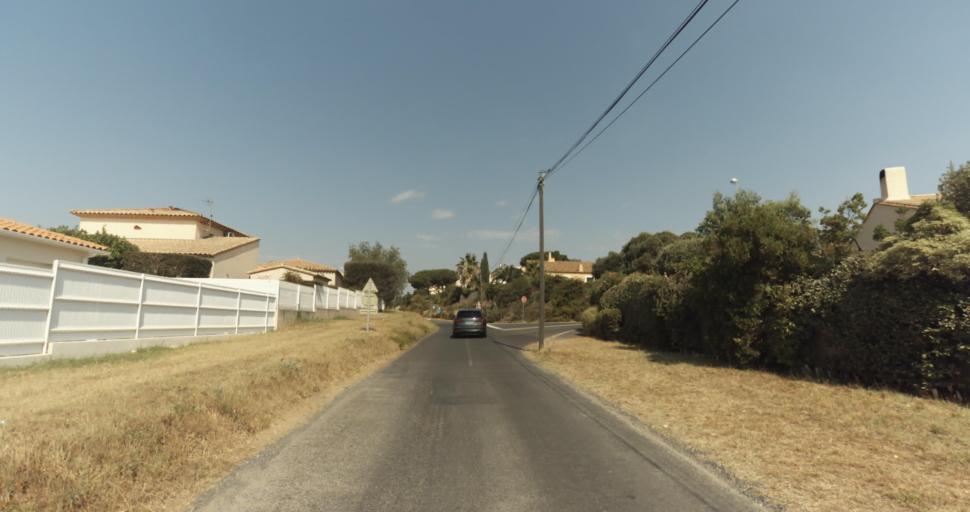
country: FR
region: Languedoc-Roussillon
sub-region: Departement des Pyrenees-Orientales
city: Latour-Bas-Elne
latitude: 42.6145
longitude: 3.0117
